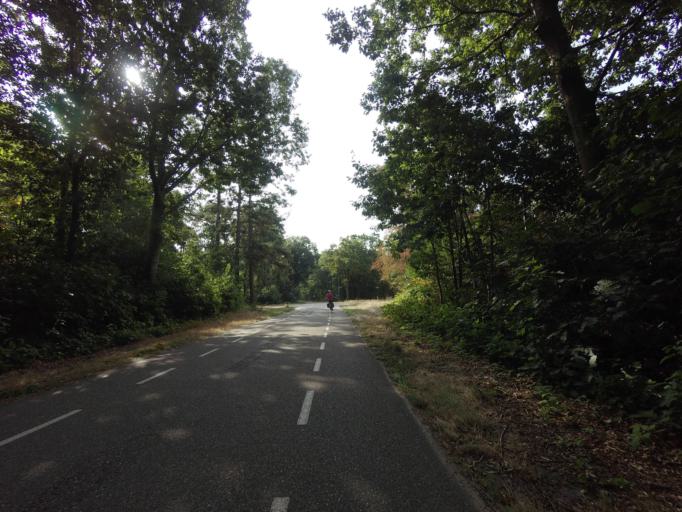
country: NL
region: North Brabant
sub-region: Gemeente Mill en Sint Hubert
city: Wilbertoord
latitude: 51.6355
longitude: 5.8200
